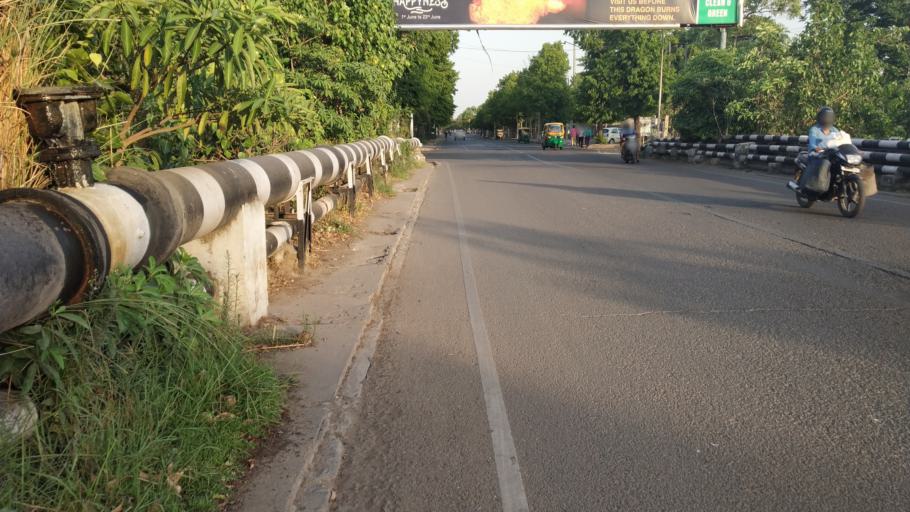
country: IN
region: Punjab
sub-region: Ajitgarh
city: Mohali
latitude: 30.6914
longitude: 76.7356
